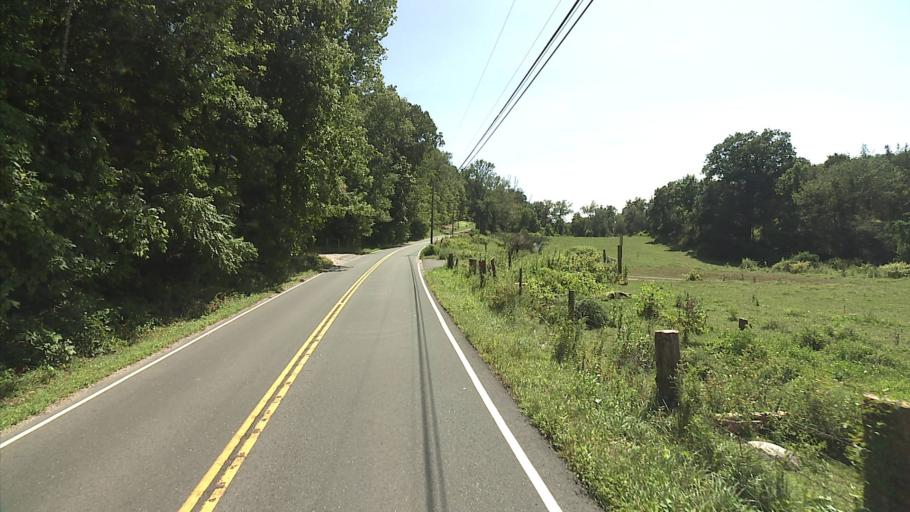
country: US
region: Connecticut
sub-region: New Haven County
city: Oxford
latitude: 41.4434
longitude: -73.1561
